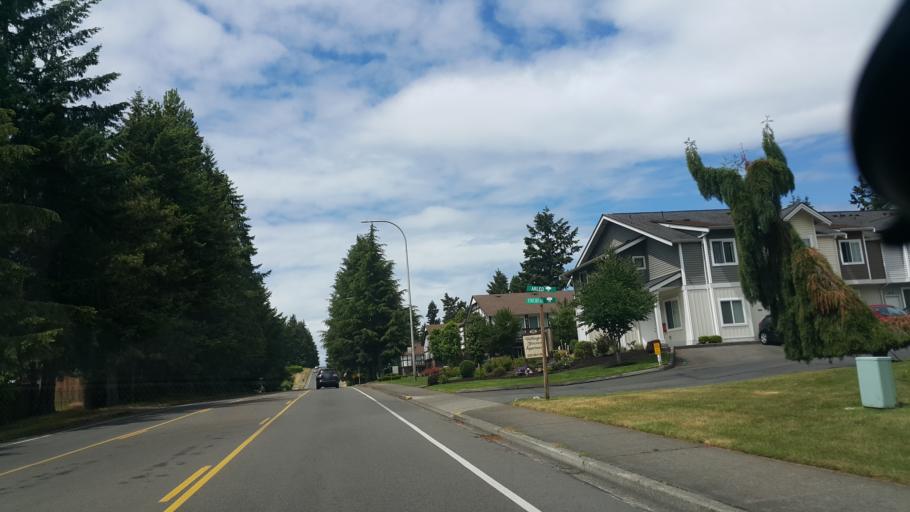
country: US
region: Washington
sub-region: Pierce County
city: Fircrest
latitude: 47.2211
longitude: -122.5180
